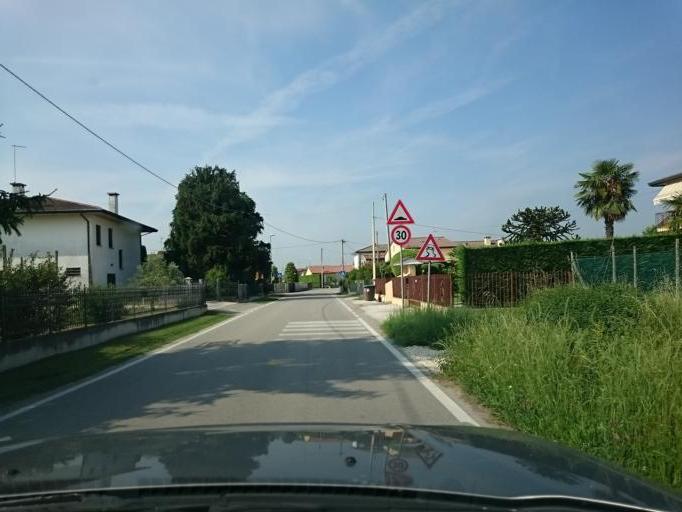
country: IT
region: Veneto
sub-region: Provincia di Padova
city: Ponte San Nicolo
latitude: 45.3606
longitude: 11.9174
